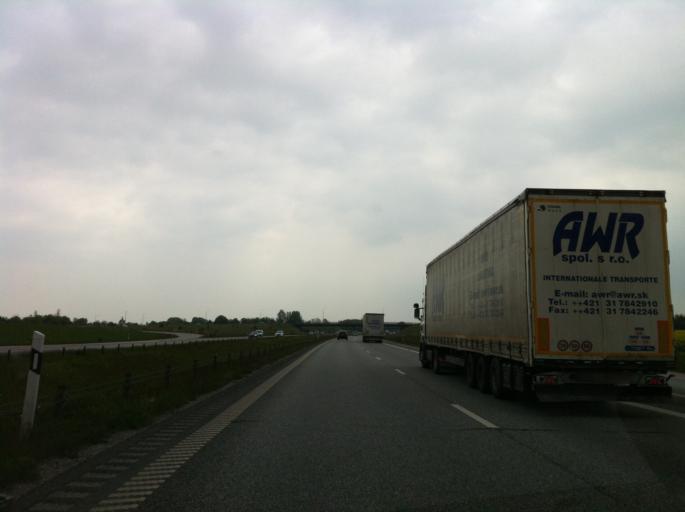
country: SE
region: Skane
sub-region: Burlovs Kommun
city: Arloev
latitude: 55.5926
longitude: 13.1166
